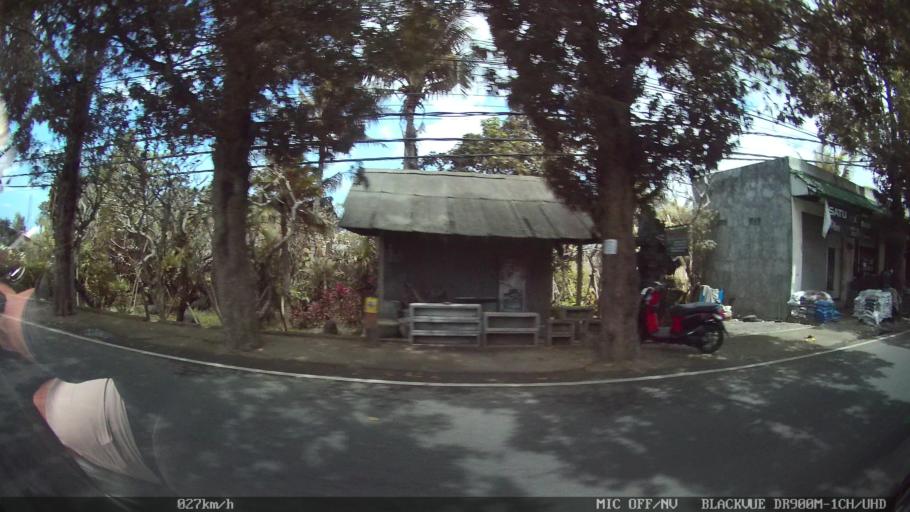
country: ID
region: Bali
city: Banjar Sedang
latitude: -8.5635
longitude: 115.2788
